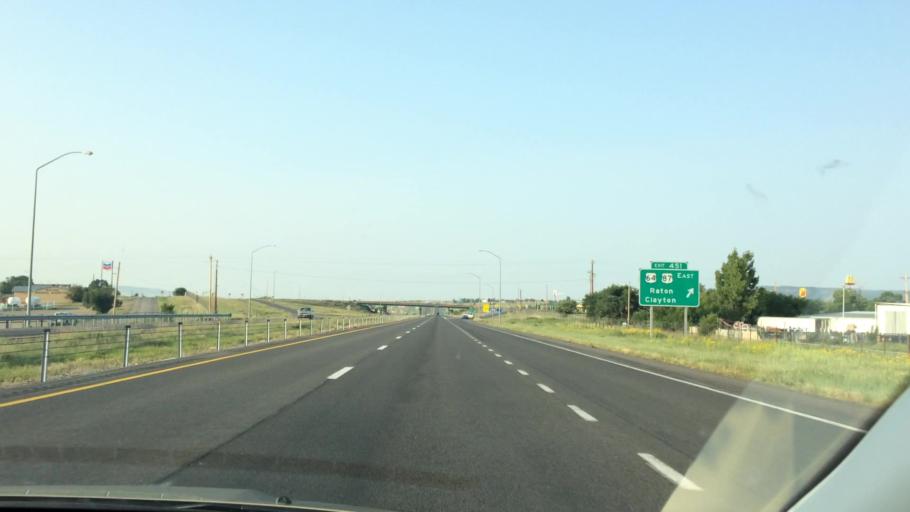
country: US
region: New Mexico
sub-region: Colfax County
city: Raton
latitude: 36.8894
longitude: -104.4294
